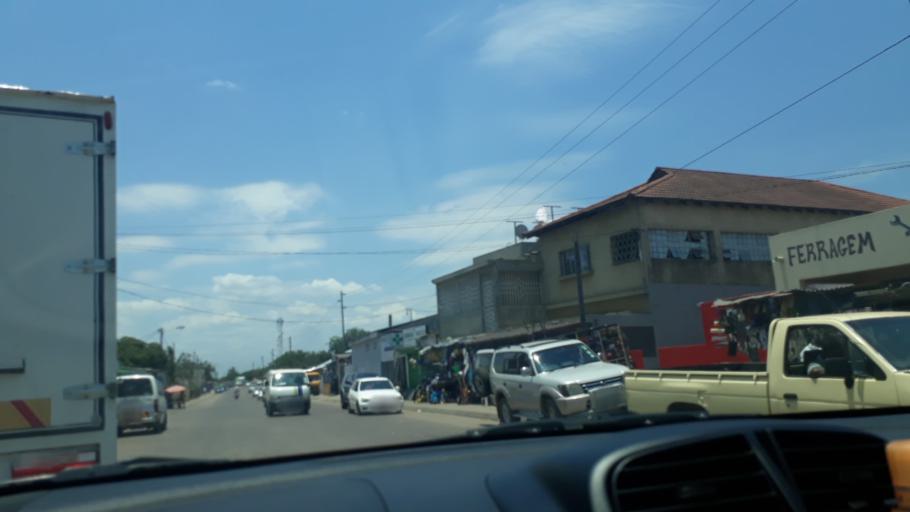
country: MZ
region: Maputo City
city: Maputo
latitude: -25.8818
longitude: 32.6050
